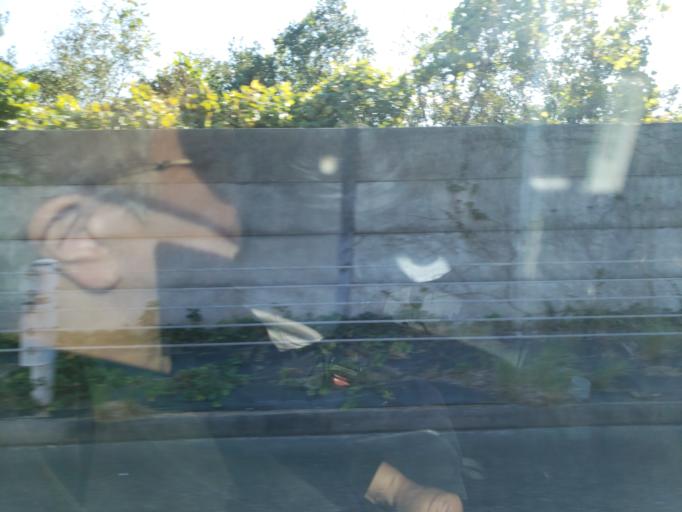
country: JP
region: Hyogo
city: Sumoto
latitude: 34.3342
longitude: 134.8328
